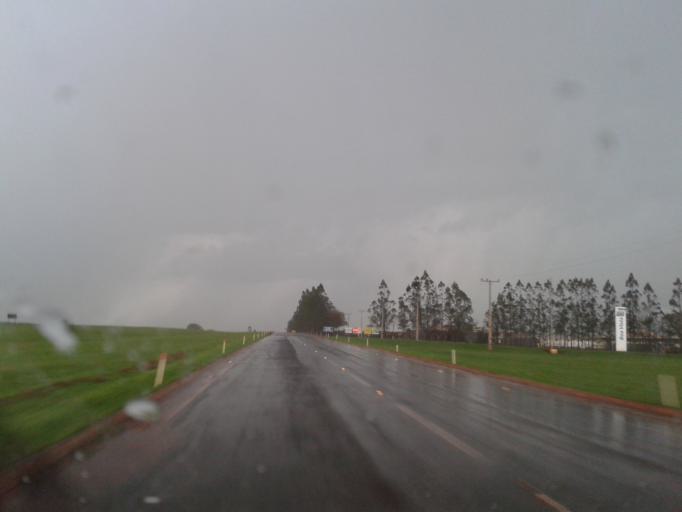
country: BR
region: Goias
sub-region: Quirinopolis
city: Quirinopolis
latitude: -18.5544
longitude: -50.4402
